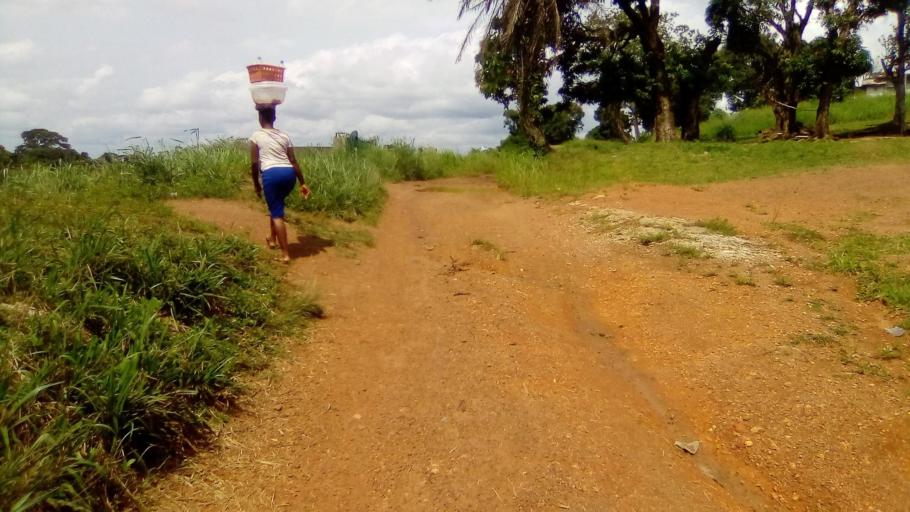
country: SL
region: Southern Province
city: Bo
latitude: 7.9766
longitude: -11.7417
